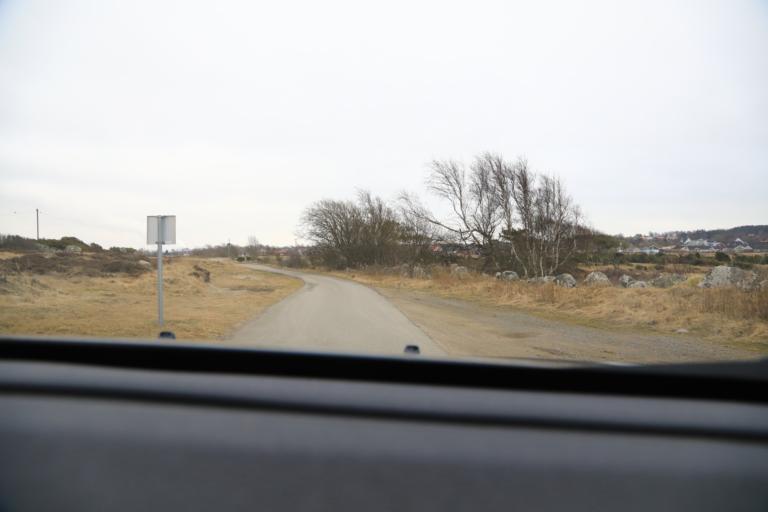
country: SE
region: Halland
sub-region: Kungsbacka Kommun
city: Frillesas
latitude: 57.2436
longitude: 12.1217
